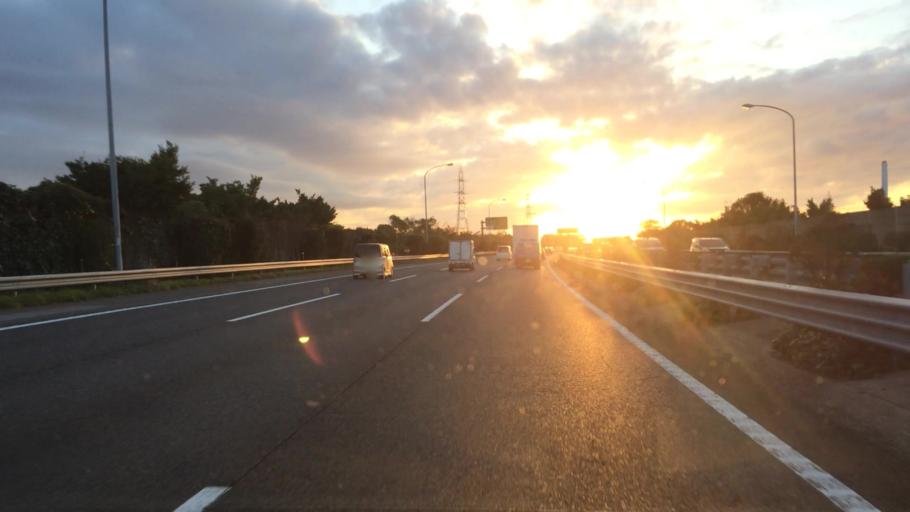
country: JP
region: Chiba
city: Yotsukaido
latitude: 35.6742
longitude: 140.1308
